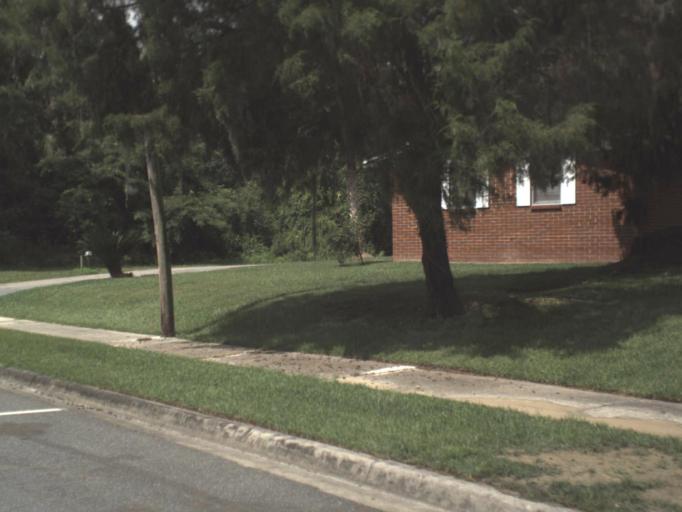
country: US
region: Florida
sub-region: Columbia County
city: Lake City
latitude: 30.1585
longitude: -82.6392
